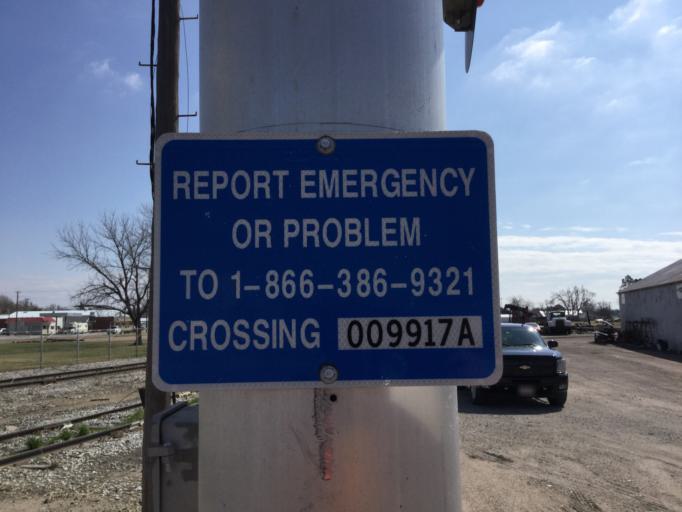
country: US
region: Kansas
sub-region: Barton County
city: Ellinwood
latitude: 38.3531
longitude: -98.5811
